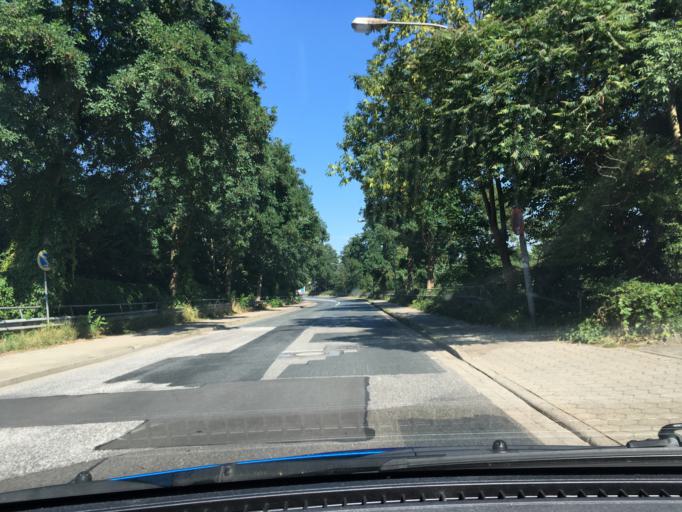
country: DE
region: Hamburg
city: Harburg
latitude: 53.4226
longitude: 10.0260
